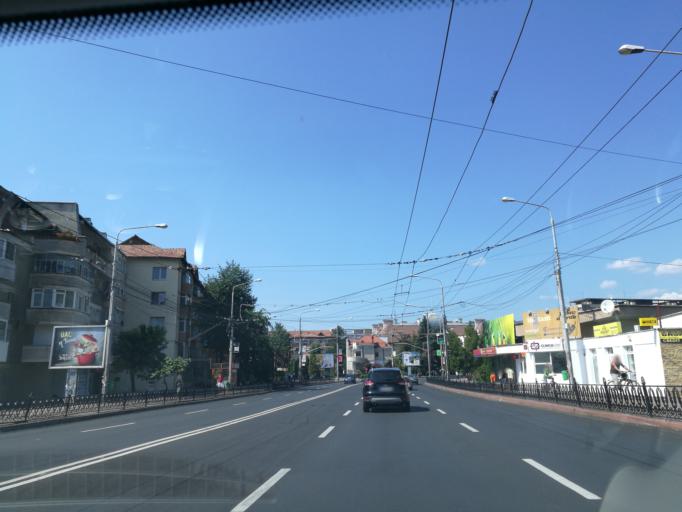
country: RO
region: Neamt
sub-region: Municipiul Piatra-Neamt
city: Valeni
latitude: 46.9270
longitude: 26.3720
